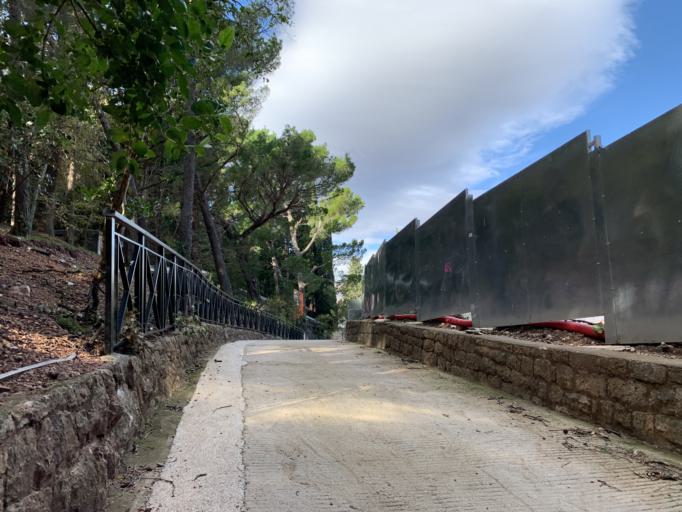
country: ME
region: Budva
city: Budva
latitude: 42.2649
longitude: 18.8923
